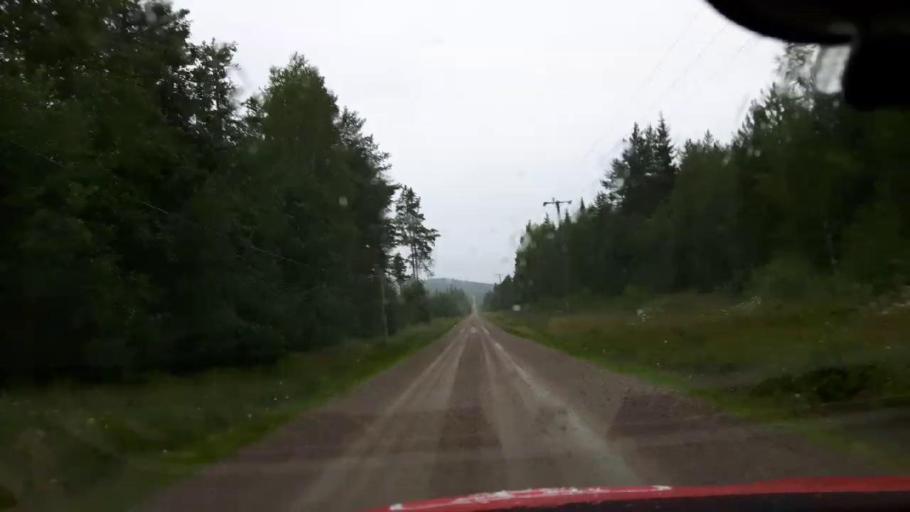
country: SE
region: Jaemtland
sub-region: OEstersunds Kommun
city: Brunflo
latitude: 62.7731
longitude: 14.9938
